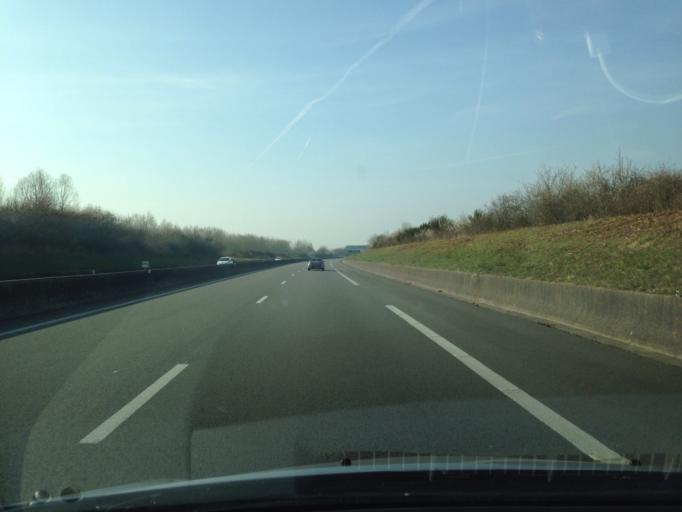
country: FR
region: Nord-Pas-de-Calais
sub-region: Departement du Pas-de-Calais
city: Saint-Josse
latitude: 50.4840
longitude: 1.6887
